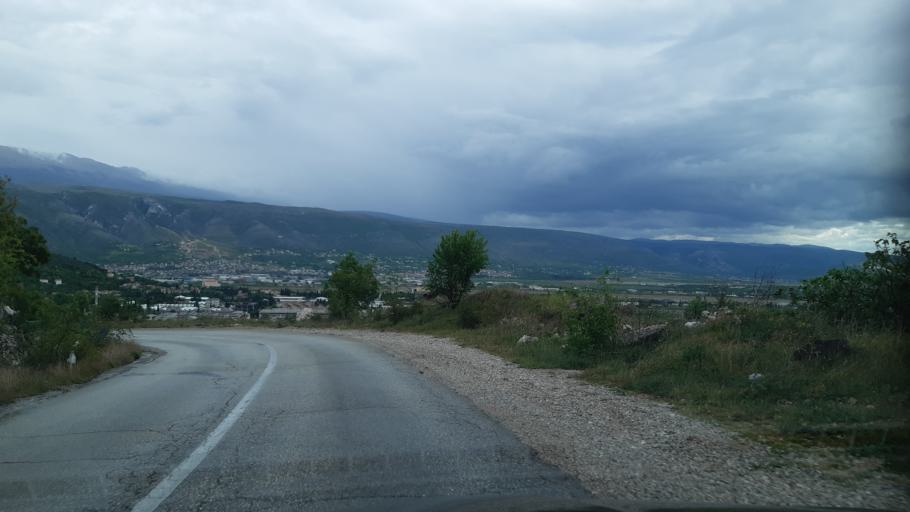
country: BA
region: Federation of Bosnia and Herzegovina
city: Rodoc
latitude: 43.3093
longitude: 17.7862
